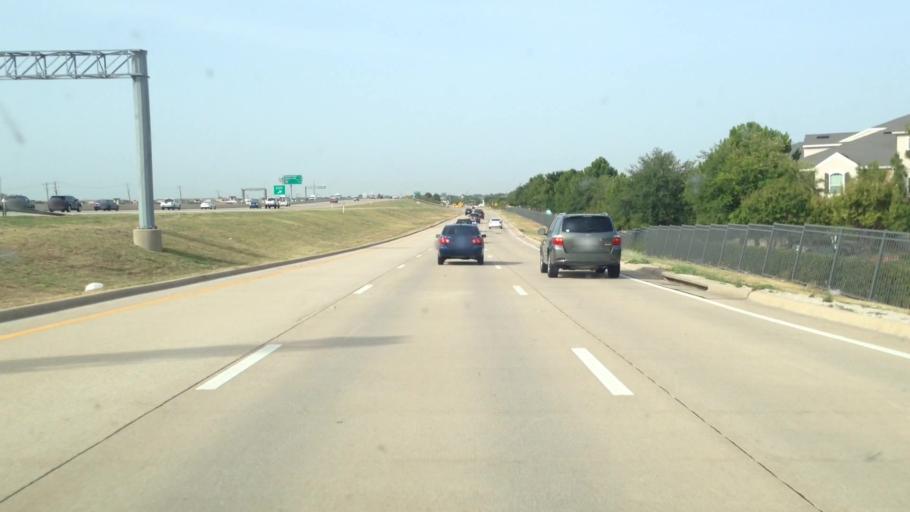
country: US
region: Texas
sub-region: Denton County
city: Lewisville
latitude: 33.0287
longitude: -96.9304
